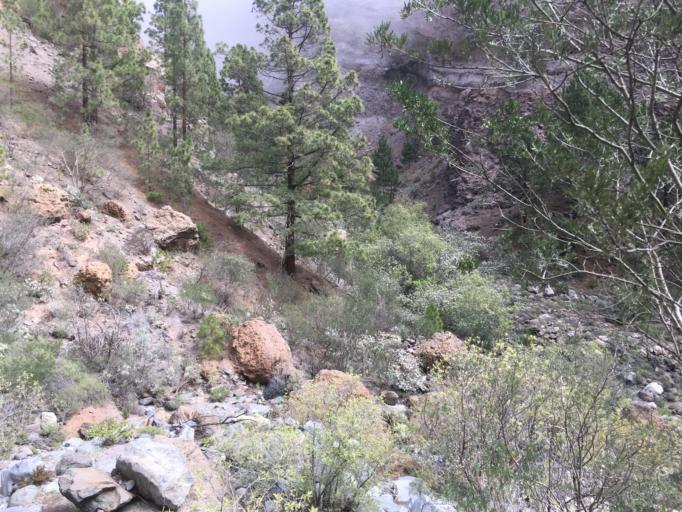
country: ES
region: Canary Islands
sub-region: Provincia de Santa Cruz de Tenerife
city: Vilaflor
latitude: 28.2011
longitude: -16.5775
